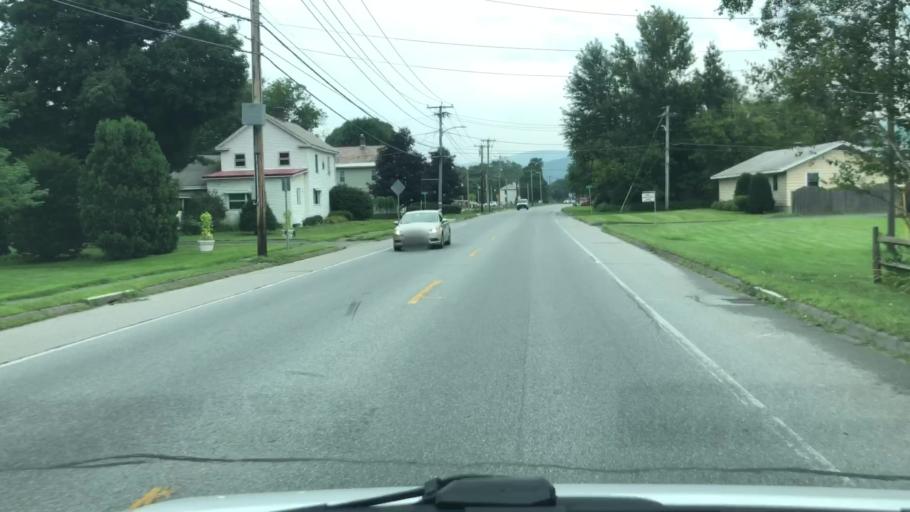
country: US
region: Massachusetts
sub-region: Berkshire County
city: Williamstown
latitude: 42.7008
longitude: -73.1690
